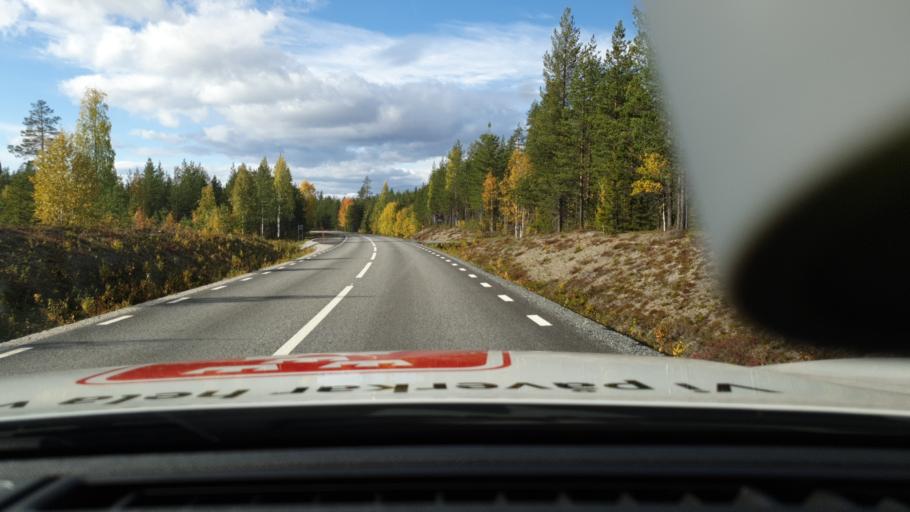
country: SE
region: Vaesterbotten
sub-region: Mala Kommun
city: Mala
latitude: 64.9828
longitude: 18.5540
